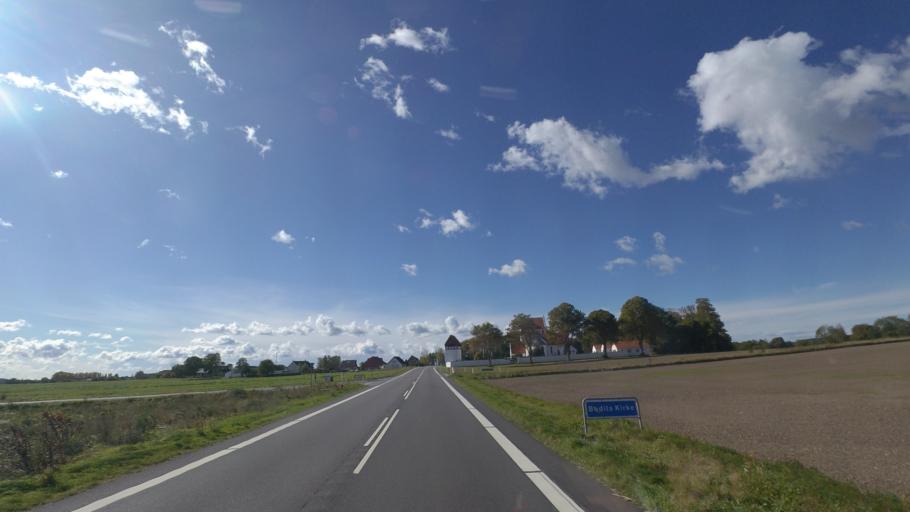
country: DK
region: Capital Region
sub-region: Bornholm Kommune
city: Nexo
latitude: 55.0620
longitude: 15.0757
